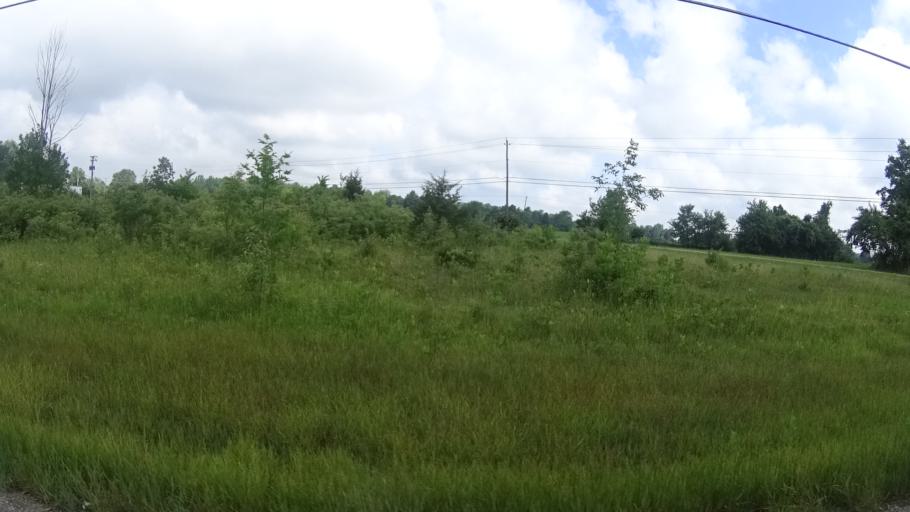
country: US
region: Ohio
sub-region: Huron County
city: Wakeman
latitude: 41.3217
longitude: -82.4184
